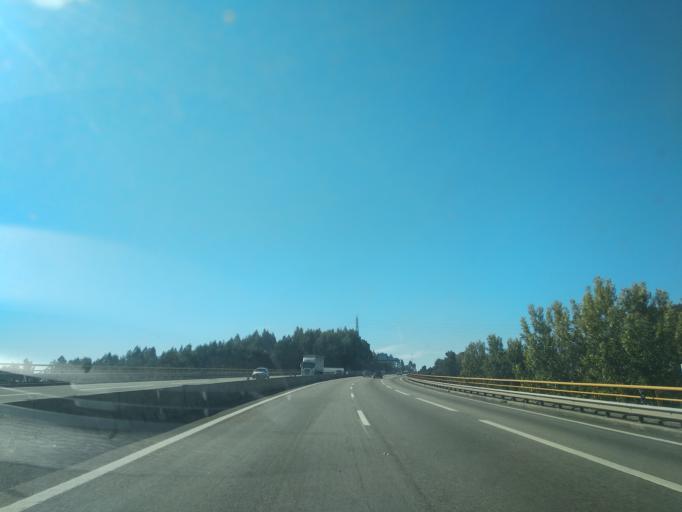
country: PT
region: Porto
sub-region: Vila Nova de Gaia
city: Perozinho
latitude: 41.0805
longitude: -8.5759
